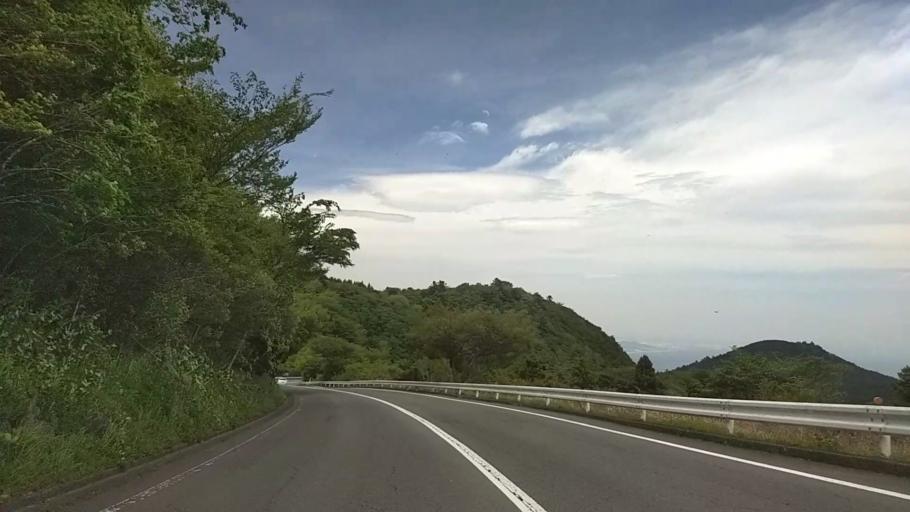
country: JP
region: Kanagawa
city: Hakone
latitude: 35.2002
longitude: 139.0832
